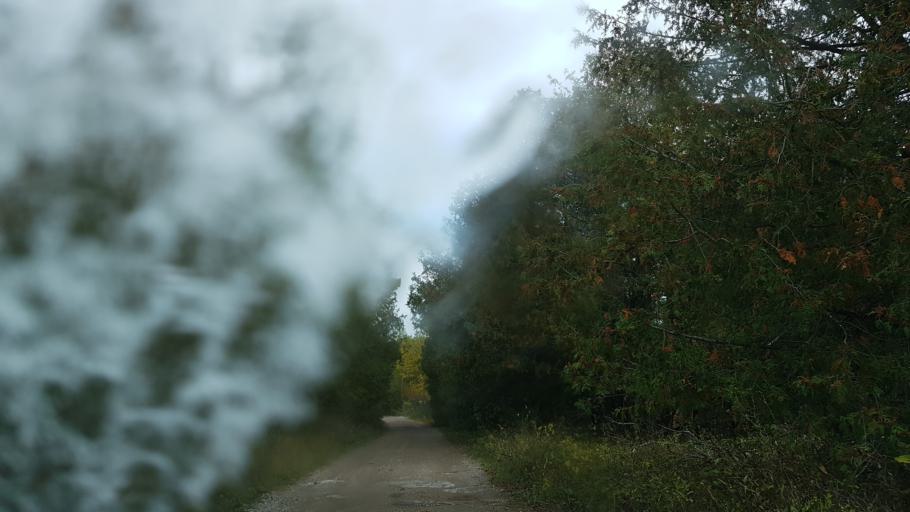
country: CA
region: Ontario
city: Gravenhurst
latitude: 44.6959
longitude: -79.0071
